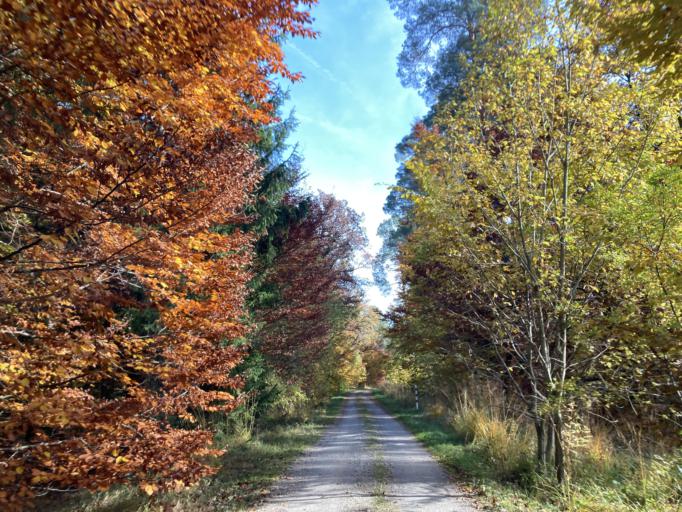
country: DE
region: Baden-Wuerttemberg
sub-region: Tuebingen Region
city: Bodelshausen
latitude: 48.4179
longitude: 8.9483
